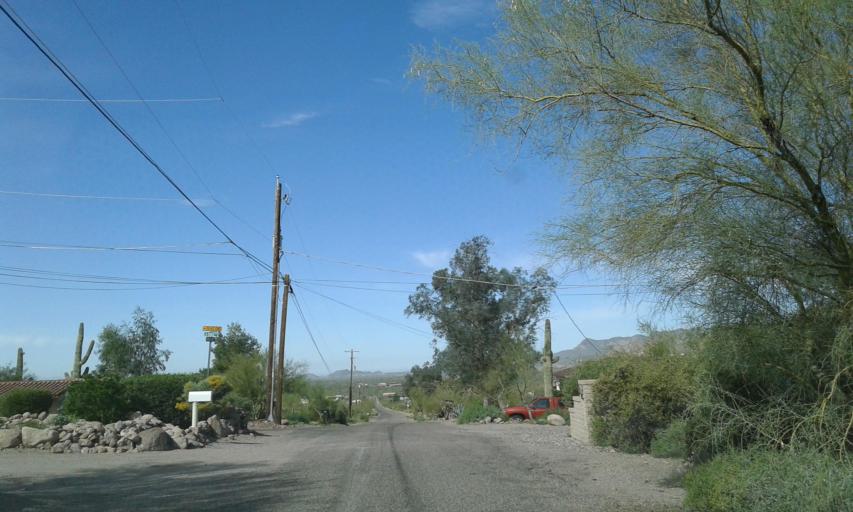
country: US
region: Arizona
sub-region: Pinal County
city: Apache Junction
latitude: 33.4496
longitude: -111.4787
